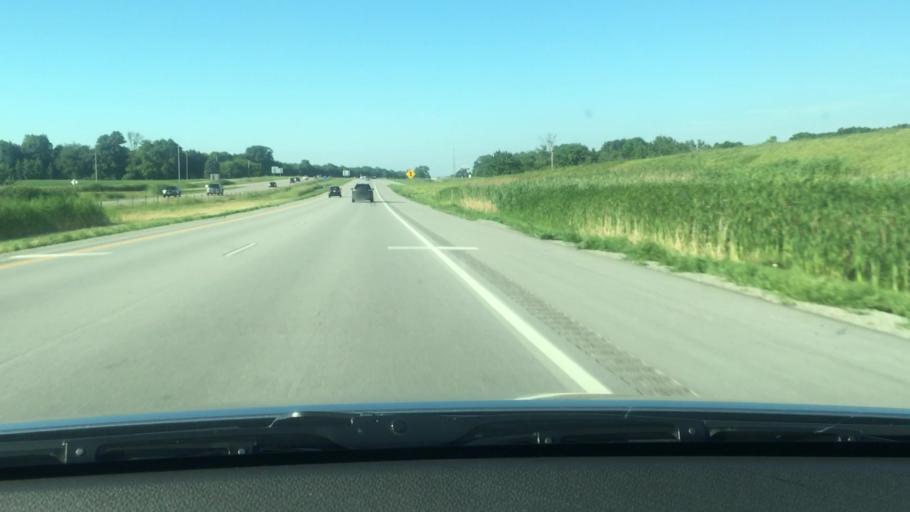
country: US
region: Wisconsin
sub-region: Brown County
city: Wrightstown
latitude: 44.3865
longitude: -88.1621
